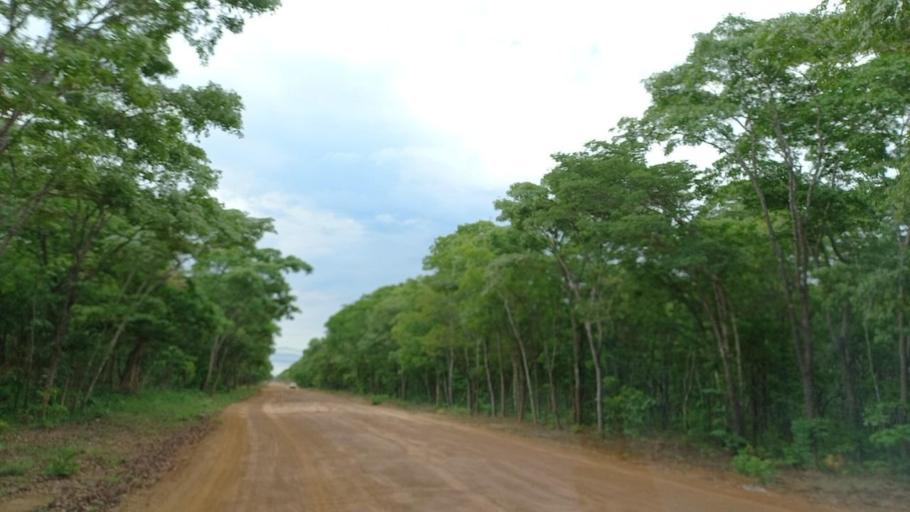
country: ZM
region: North-Western
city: Kalengwa
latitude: -13.3670
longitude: 25.0747
